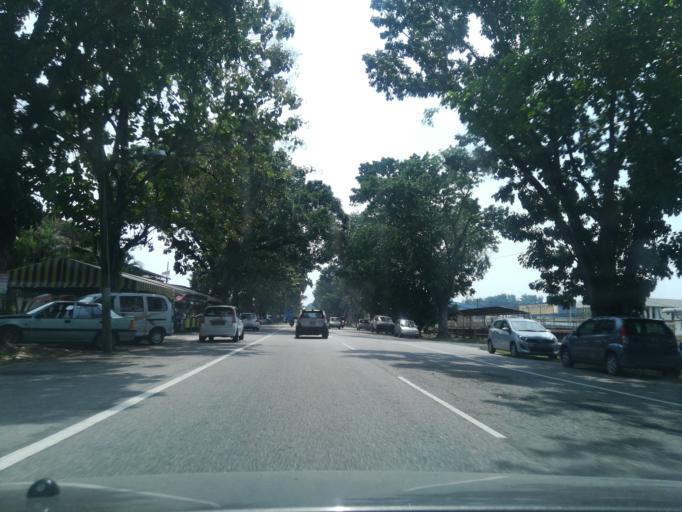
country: MY
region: Kedah
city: Kulim
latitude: 5.4096
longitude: 100.5594
